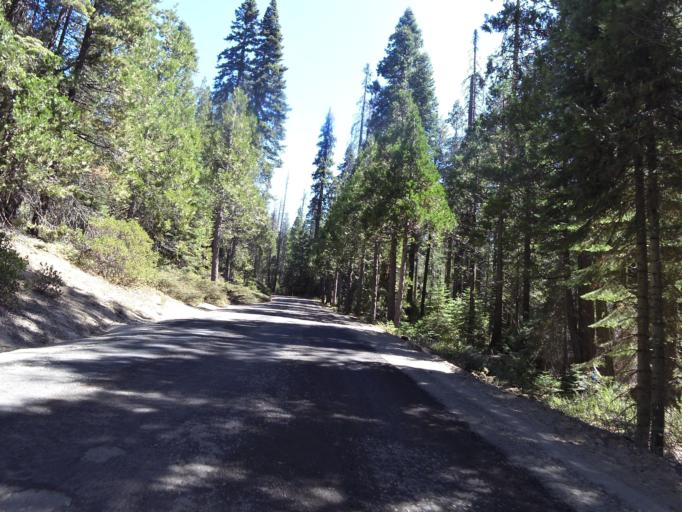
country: US
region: California
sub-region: Madera County
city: Oakhurst
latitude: 37.4118
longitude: -119.5713
